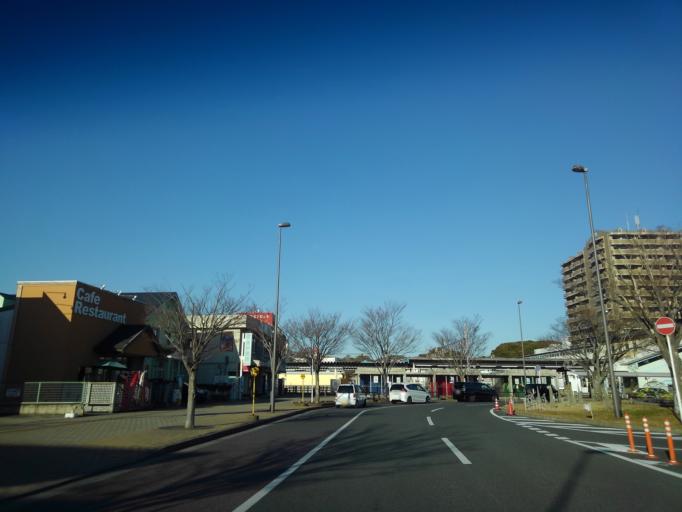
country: JP
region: Chiba
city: Kimitsu
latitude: 35.3330
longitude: 139.8941
